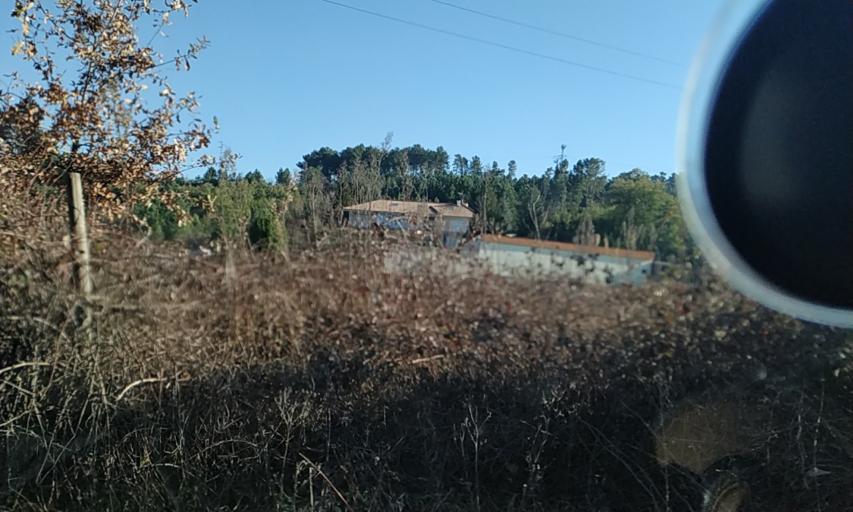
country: PT
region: Vila Real
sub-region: Vila Real
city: Vila Real
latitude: 41.2884
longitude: -7.7256
